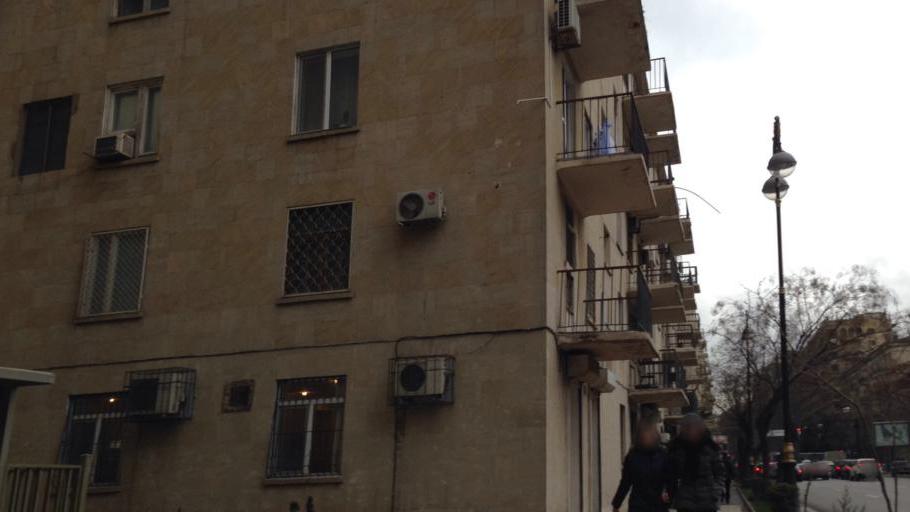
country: AZ
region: Baki
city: Baku
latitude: 40.3767
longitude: 49.8582
